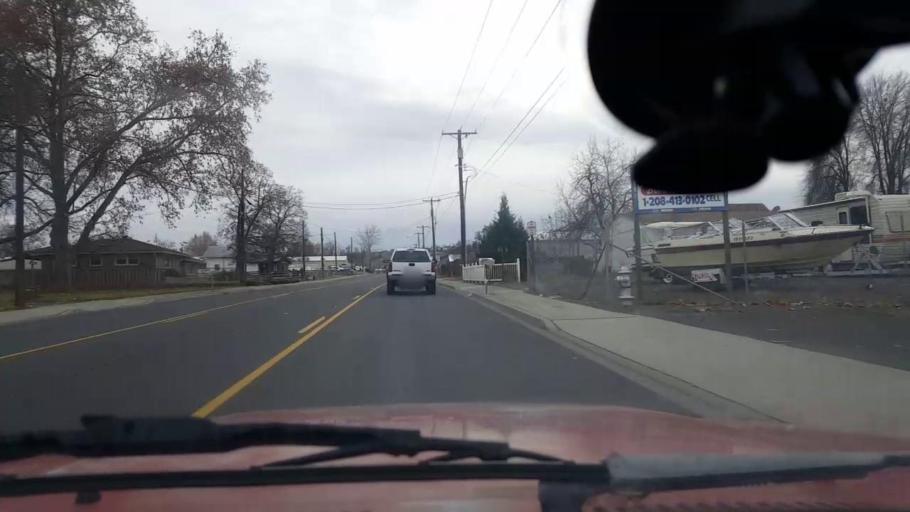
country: US
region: Washington
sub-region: Asotin County
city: West Clarkston-Highland
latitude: 46.4069
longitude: -117.0691
